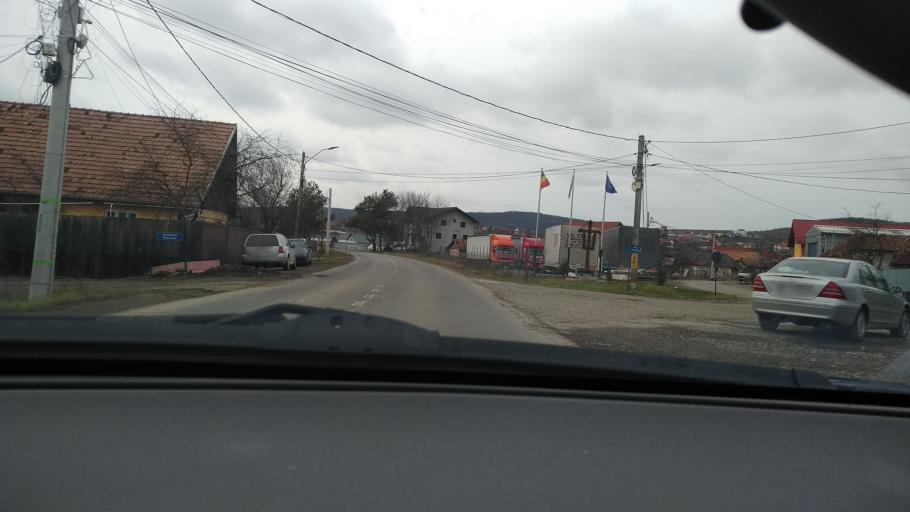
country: RO
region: Mures
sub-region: Comuna Livezeni
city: Livezeni
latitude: 46.5470
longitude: 24.6370
